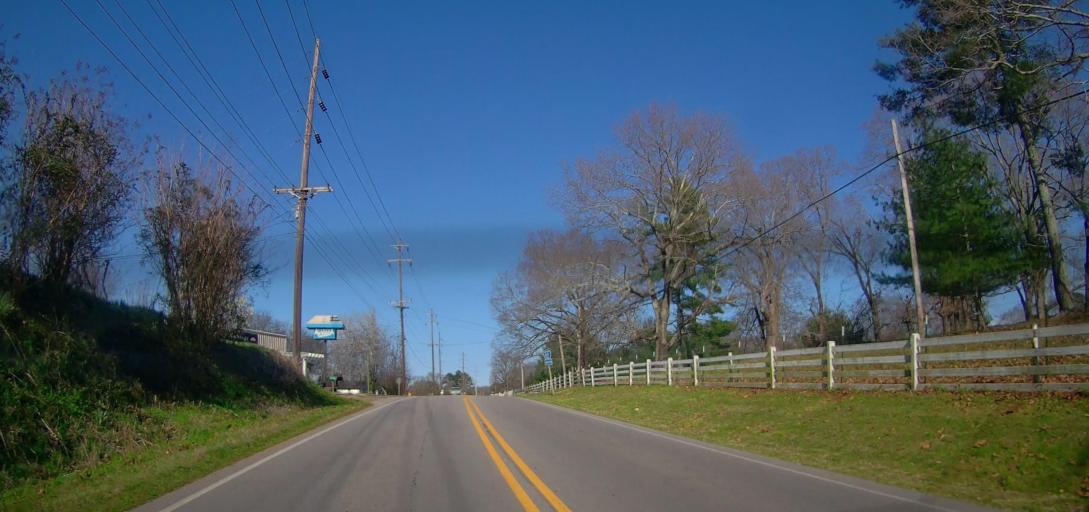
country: US
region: Alabama
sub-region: Lauderdale County
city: East Florence
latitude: 34.8275
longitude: -87.6212
